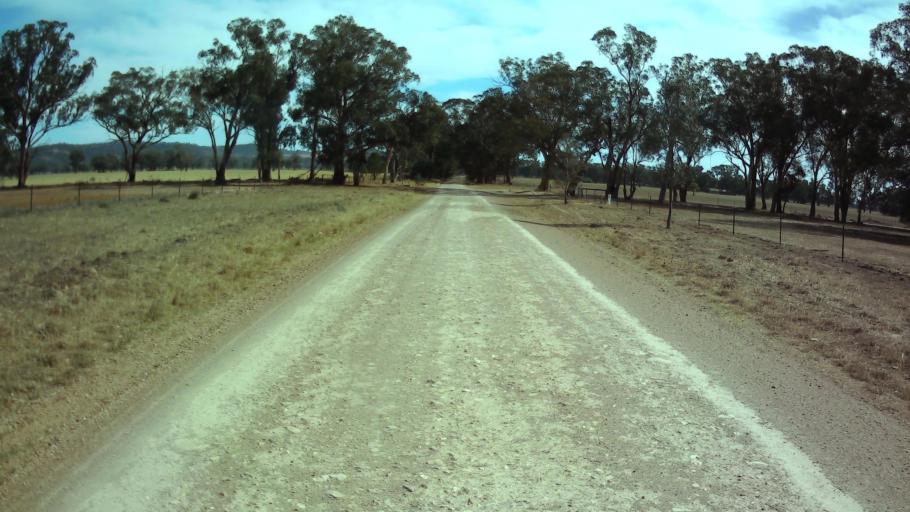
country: AU
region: New South Wales
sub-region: Weddin
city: Grenfell
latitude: -33.7004
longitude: 148.3022
